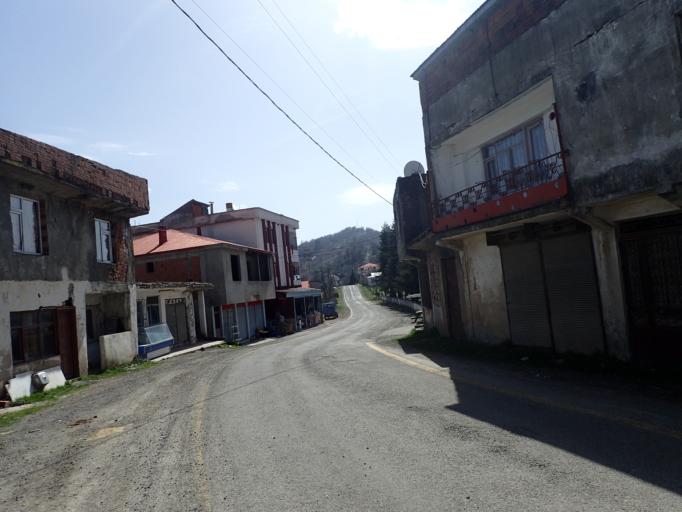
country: TR
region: Ordu
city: Kabaduz
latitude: 40.8206
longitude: 37.9044
